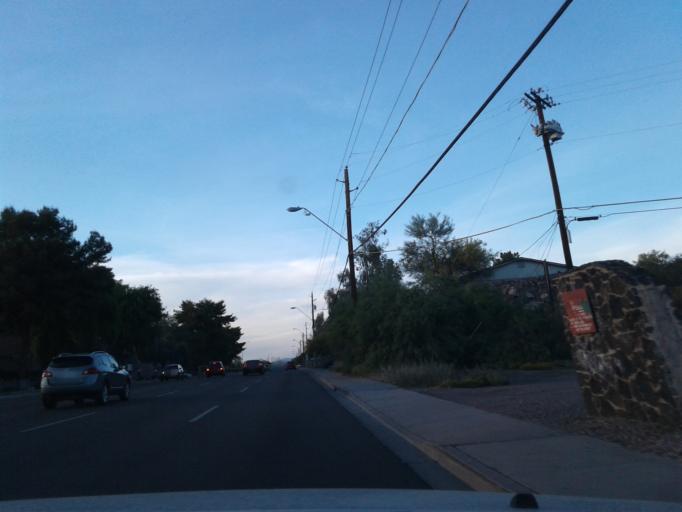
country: US
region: Arizona
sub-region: Maricopa County
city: Glendale
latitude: 33.6160
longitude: -112.0996
